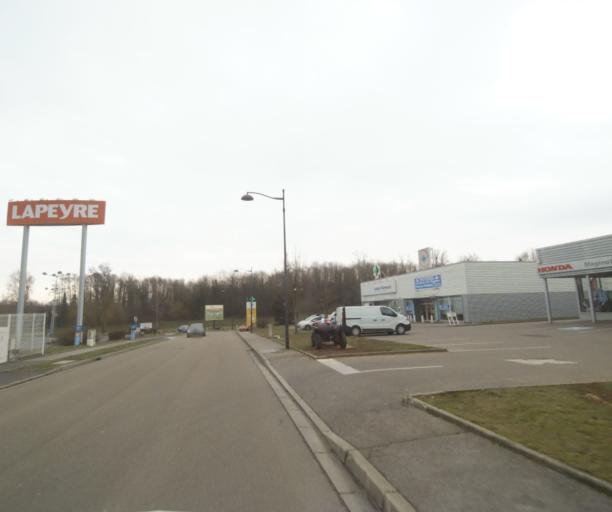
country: FR
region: Champagne-Ardenne
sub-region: Departement de la Haute-Marne
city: Saint-Dizier
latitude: 48.6245
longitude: 4.9707
